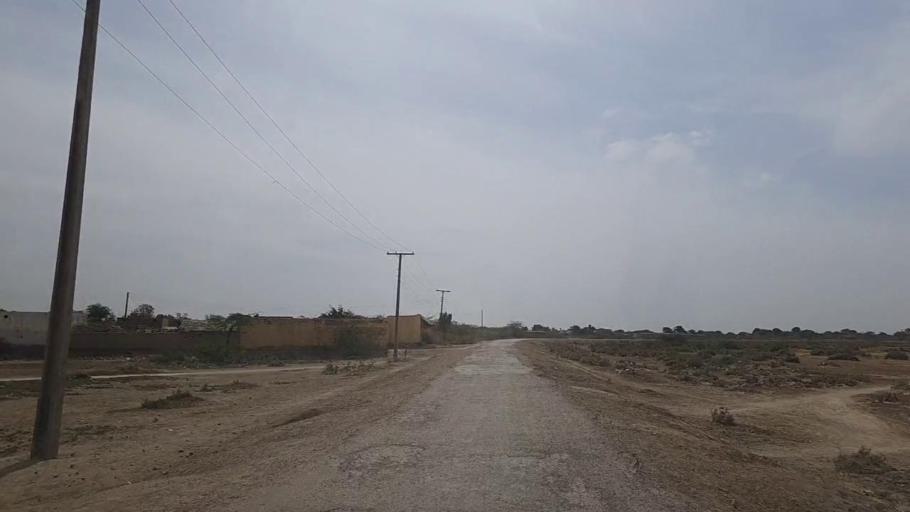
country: PK
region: Sindh
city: Kunri
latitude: 25.2143
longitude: 69.5033
